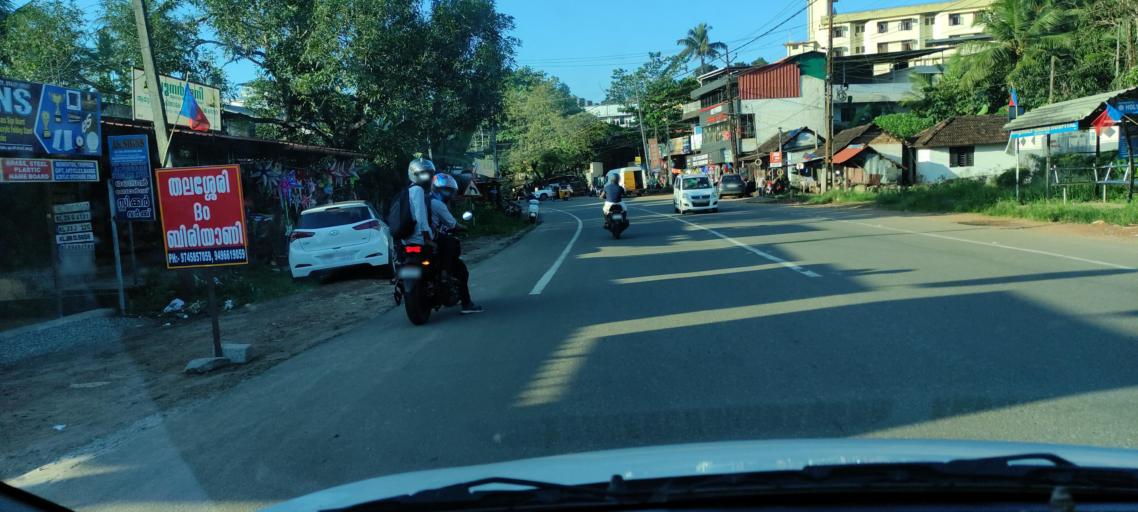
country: IN
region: Kerala
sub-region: Pattanamtitta
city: Adur
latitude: 9.1605
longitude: 76.7242
